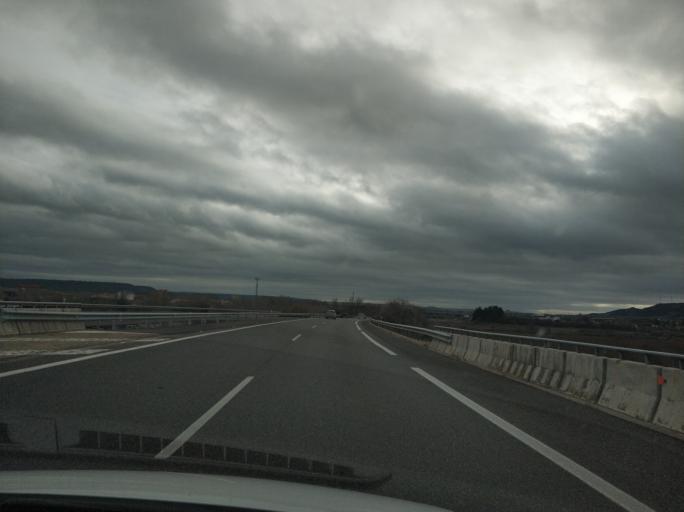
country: ES
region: Castille and Leon
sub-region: Provincia de Palencia
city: Venta de Banos
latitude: 41.9302
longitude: -4.4986
